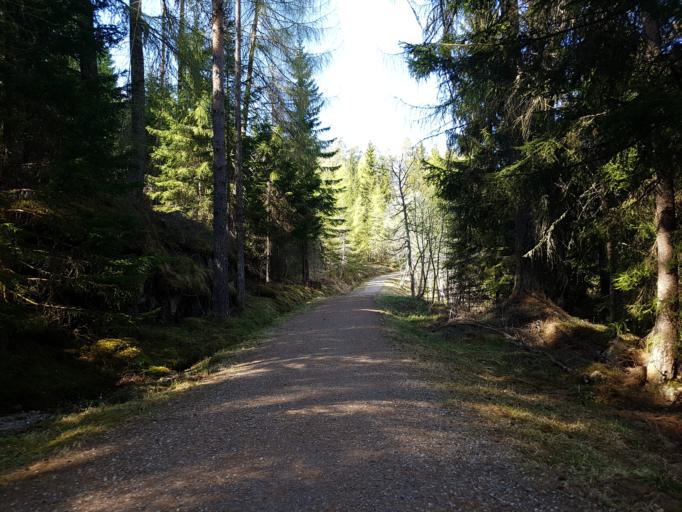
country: NO
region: Sor-Trondelag
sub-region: Trondheim
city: Trondheim
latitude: 63.4354
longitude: 10.3443
